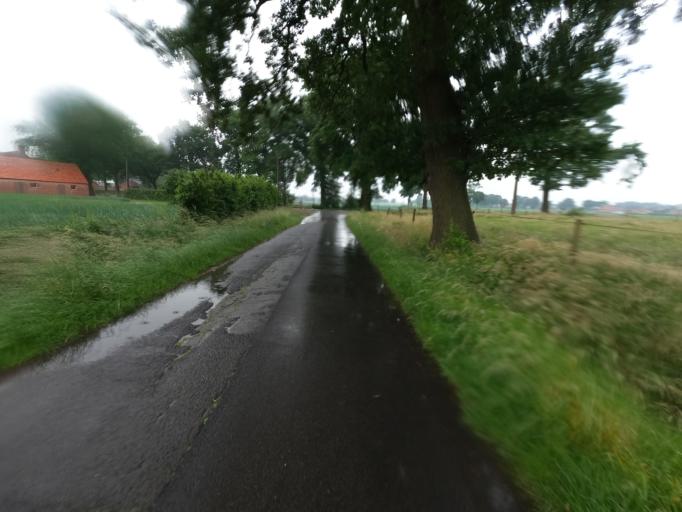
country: BE
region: Flanders
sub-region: Provincie Antwerpen
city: Kalmthout
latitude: 51.3917
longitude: 4.5131
